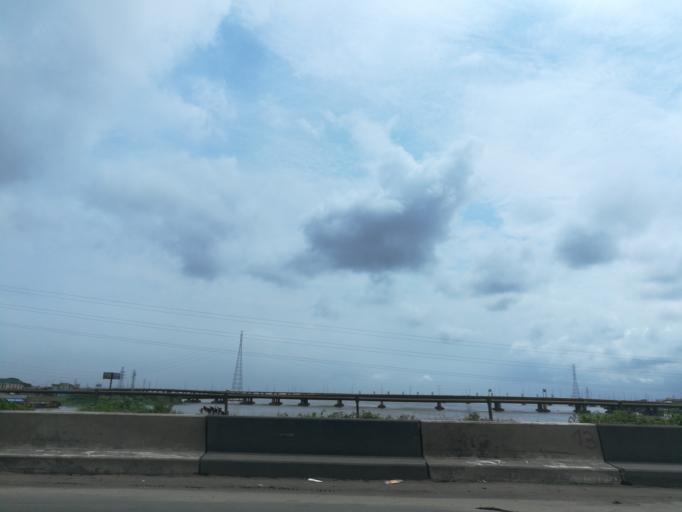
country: NG
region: Lagos
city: Lagos
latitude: 6.4648
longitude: 3.3801
